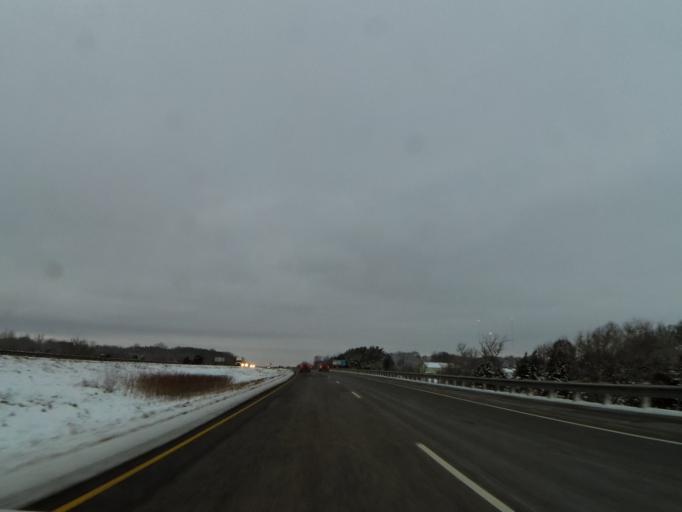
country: US
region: Wisconsin
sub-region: Saint Croix County
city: Hudson
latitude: 44.9651
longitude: -92.6584
